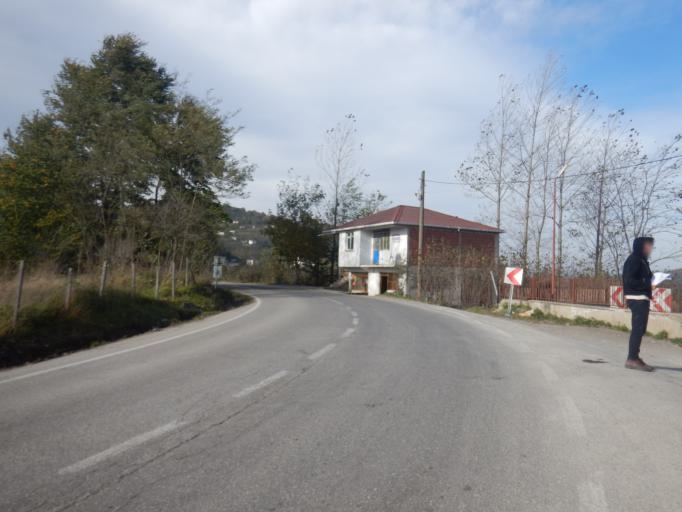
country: TR
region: Ordu
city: Golkoy
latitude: 40.6912
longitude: 37.5967
